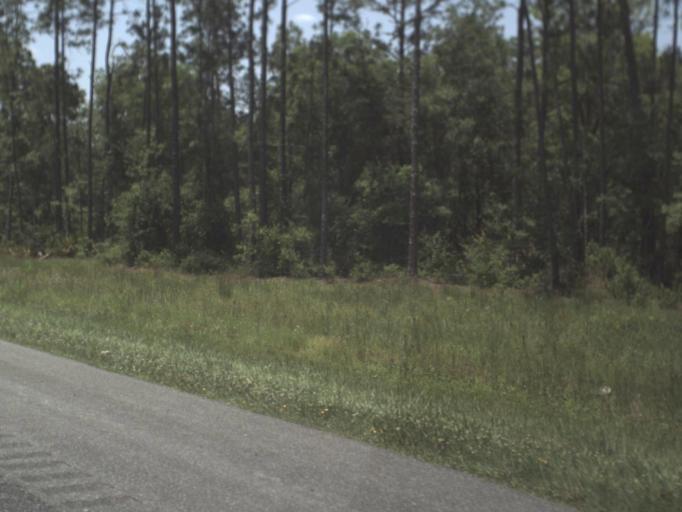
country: US
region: Florida
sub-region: Columbia County
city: Five Points
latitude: 30.2414
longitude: -82.6241
